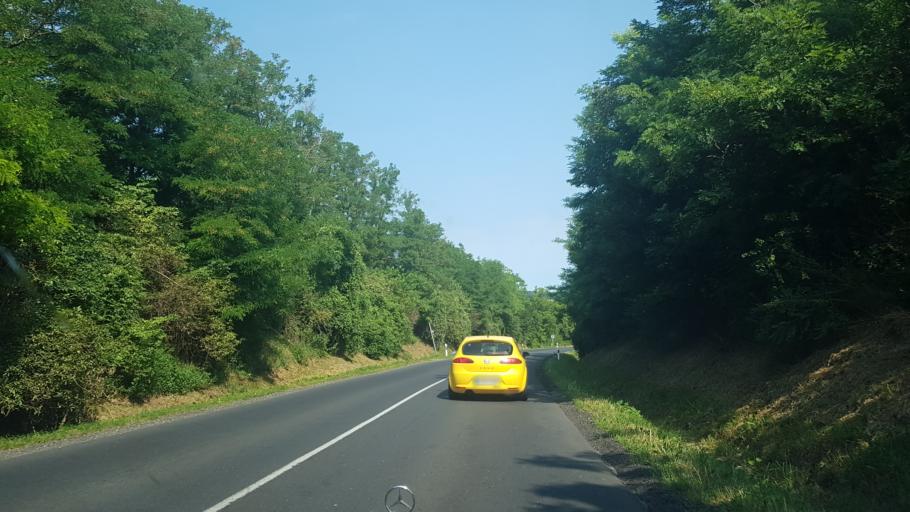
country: HU
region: Somogy
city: Bohonye
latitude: 46.4535
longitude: 17.3715
